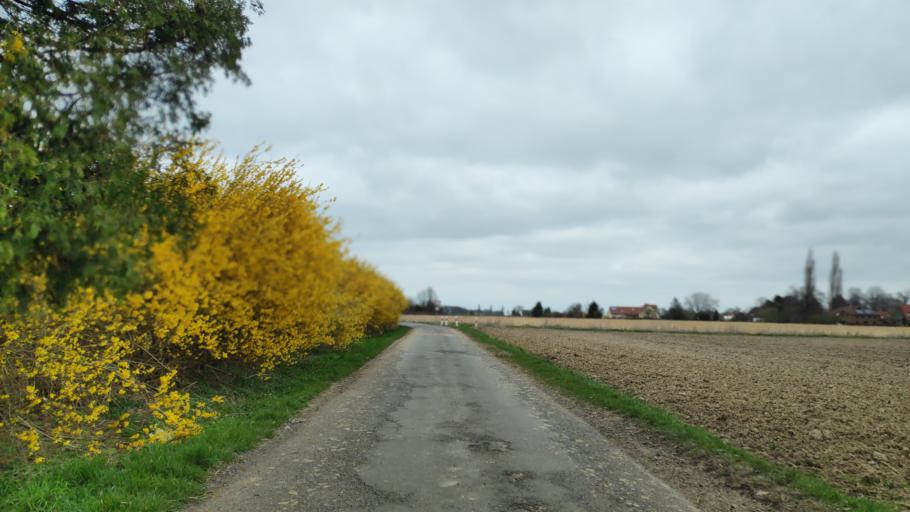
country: DE
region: North Rhine-Westphalia
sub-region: Regierungsbezirk Detmold
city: Minden
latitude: 52.3214
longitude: 8.8469
